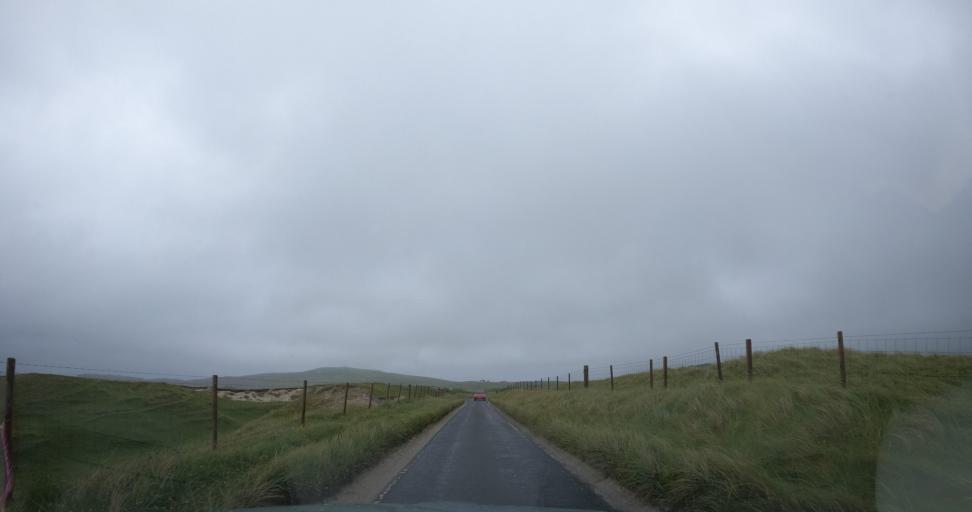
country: GB
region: Scotland
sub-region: Eilean Siar
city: Barra
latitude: 56.9956
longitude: -7.5070
